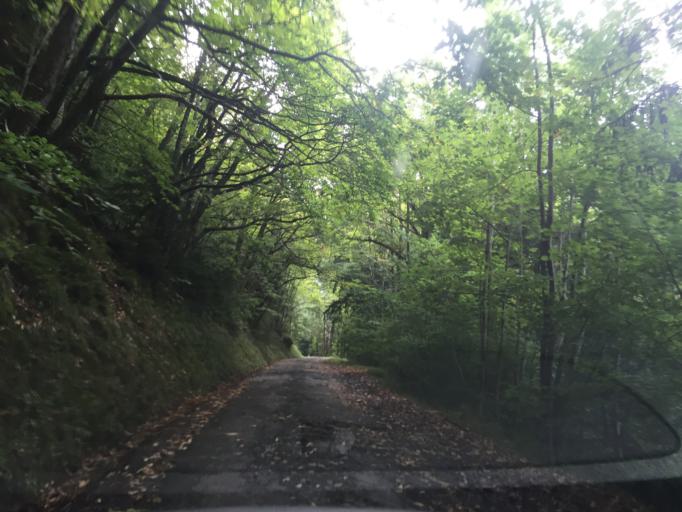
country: FR
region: Rhone-Alpes
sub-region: Departement de la Savoie
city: La Rochette
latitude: 45.4403
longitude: 6.1528
